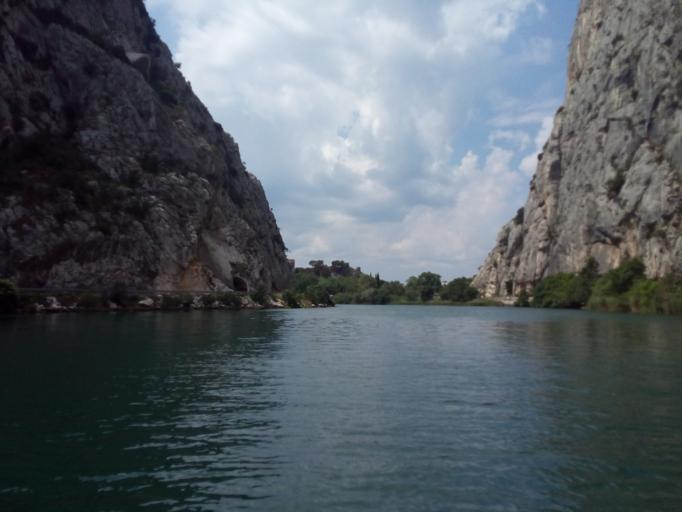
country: HR
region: Splitsko-Dalmatinska
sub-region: Grad Omis
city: Omis
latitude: 43.4508
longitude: 16.6953
